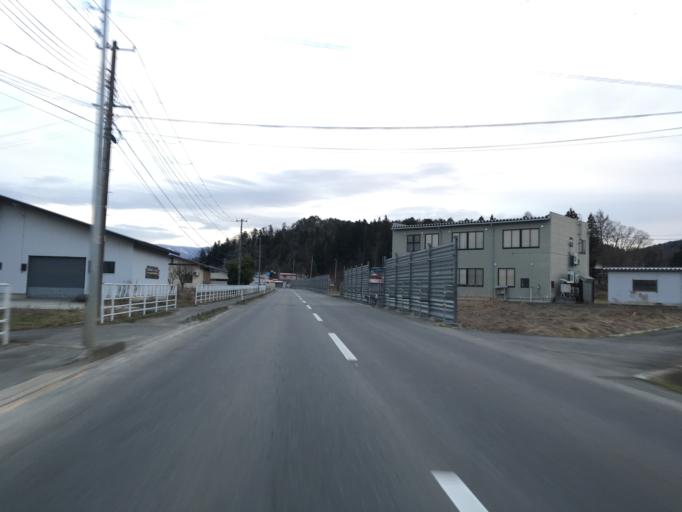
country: JP
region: Yamagata
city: Yonezawa
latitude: 37.9476
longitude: 140.0724
